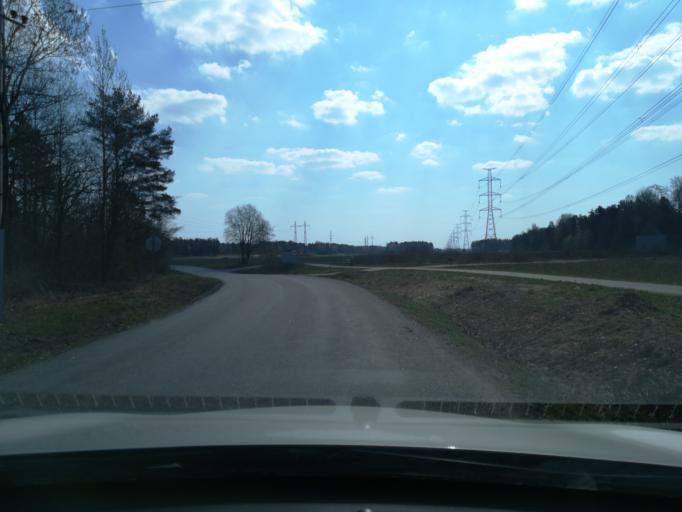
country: EE
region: Harju
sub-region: Saue vald
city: Laagri
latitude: 59.3507
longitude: 24.5923
